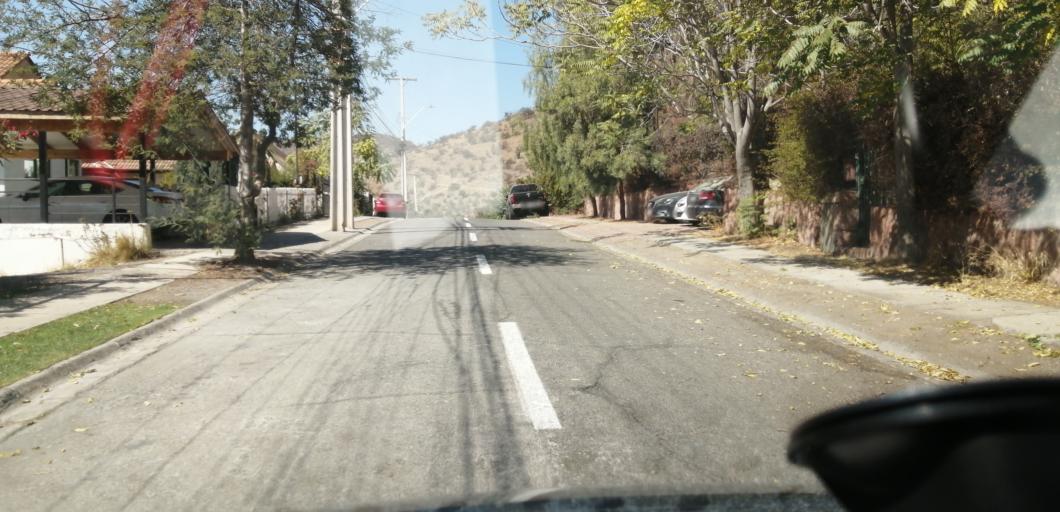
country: CL
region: Santiago Metropolitan
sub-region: Provincia de Santiago
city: Lo Prado
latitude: -33.4584
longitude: -70.8224
